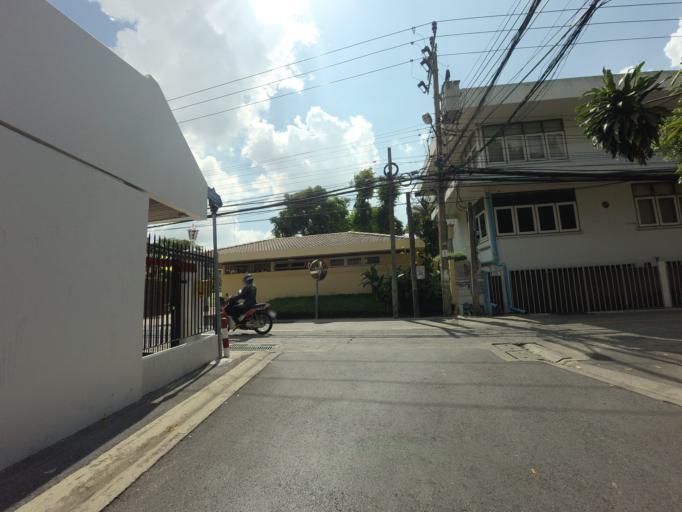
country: TH
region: Bangkok
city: Phaya Thai
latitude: 13.7807
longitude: 100.5516
